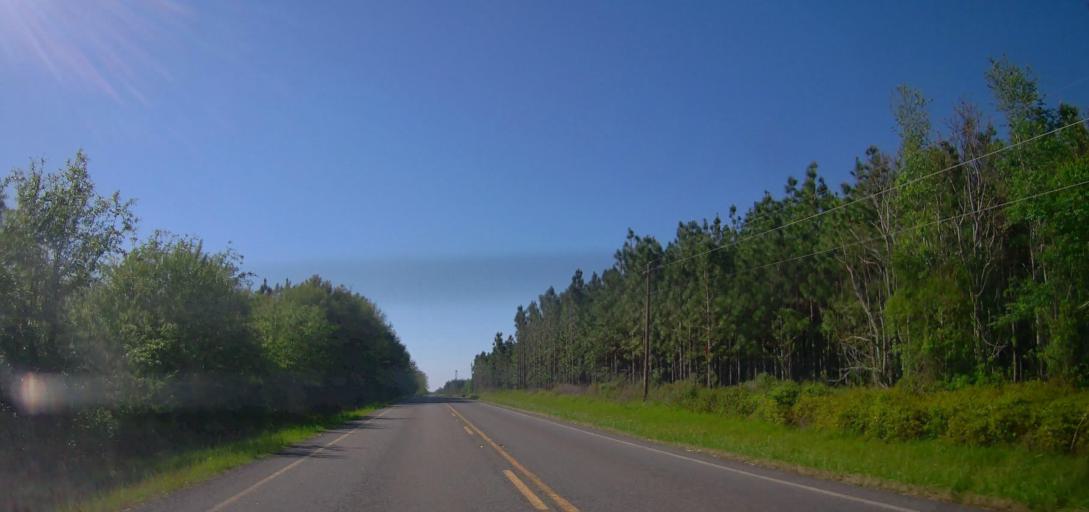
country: US
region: Georgia
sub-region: Wilcox County
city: Rochelle
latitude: 31.9959
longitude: -83.4739
